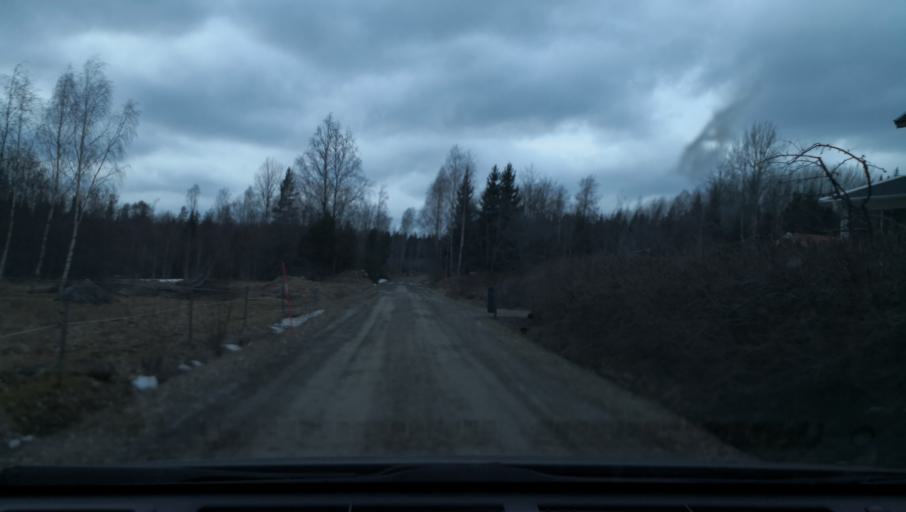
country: SE
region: OErebro
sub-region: Lindesbergs Kommun
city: Fellingsbro
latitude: 59.5998
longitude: 15.6209
